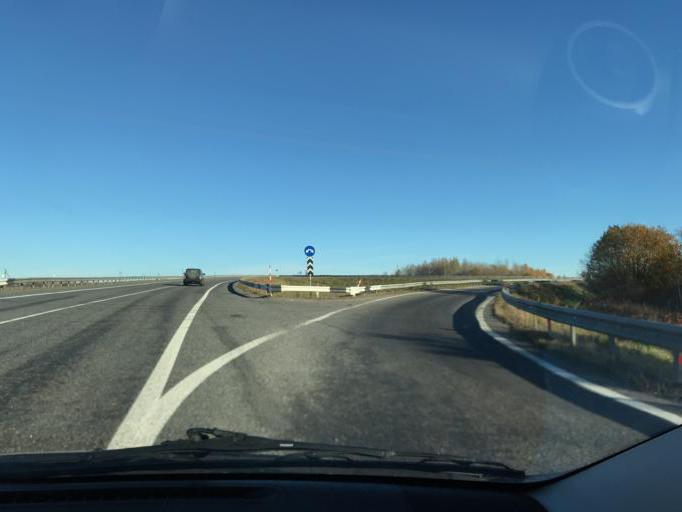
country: BY
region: Vitebsk
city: Vitebsk
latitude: 55.0991
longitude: 30.3000
